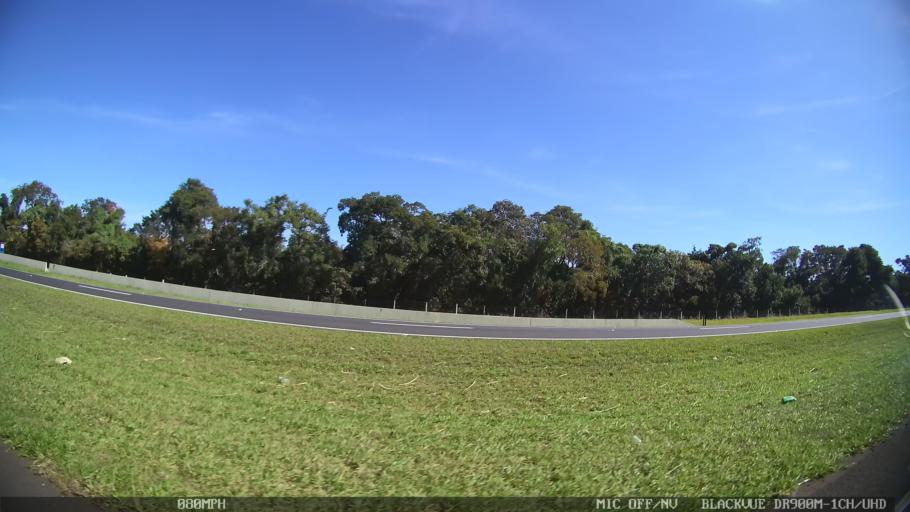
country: BR
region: Sao Paulo
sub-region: Santa Rita Do Passa Quatro
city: Santa Rita do Passa Quatro
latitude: -21.6290
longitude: -47.6139
